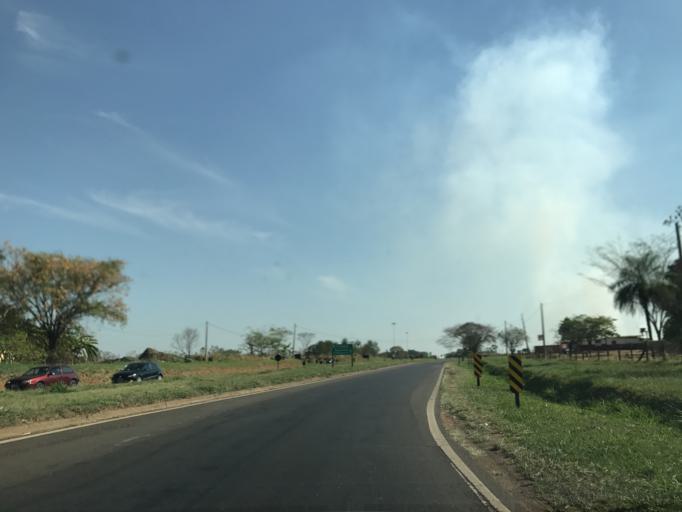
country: BR
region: Sao Paulo
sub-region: Penapolis
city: Penapolis
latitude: -21.3852
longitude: -50.0949
